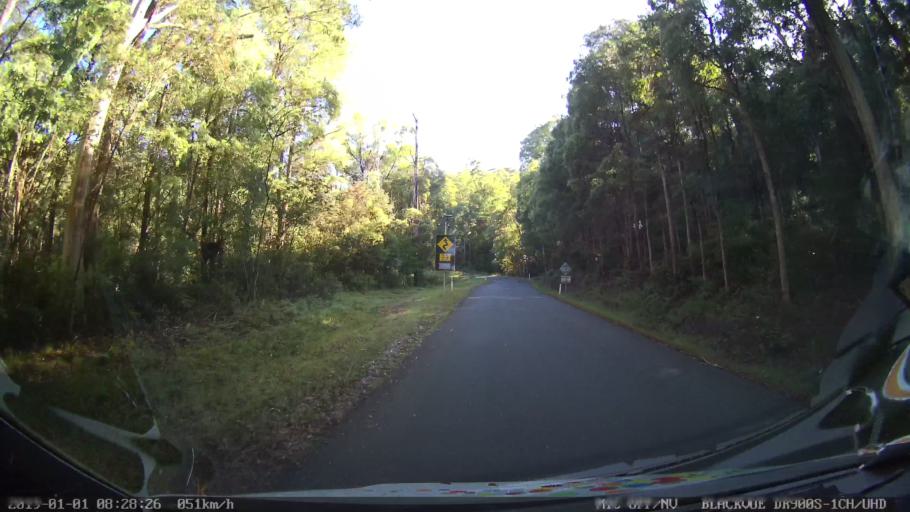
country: AU
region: New South Wales
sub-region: Snowy River
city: Jindabyne
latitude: -36.3766
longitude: 148.1897
